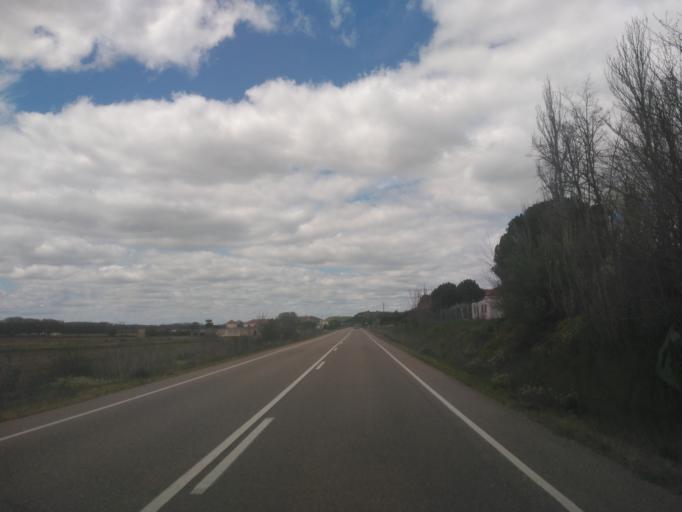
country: ES
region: Castille and Leon
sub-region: Provincia de Salamanca
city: Valverdon
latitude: 41.0512
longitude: -5.7889
